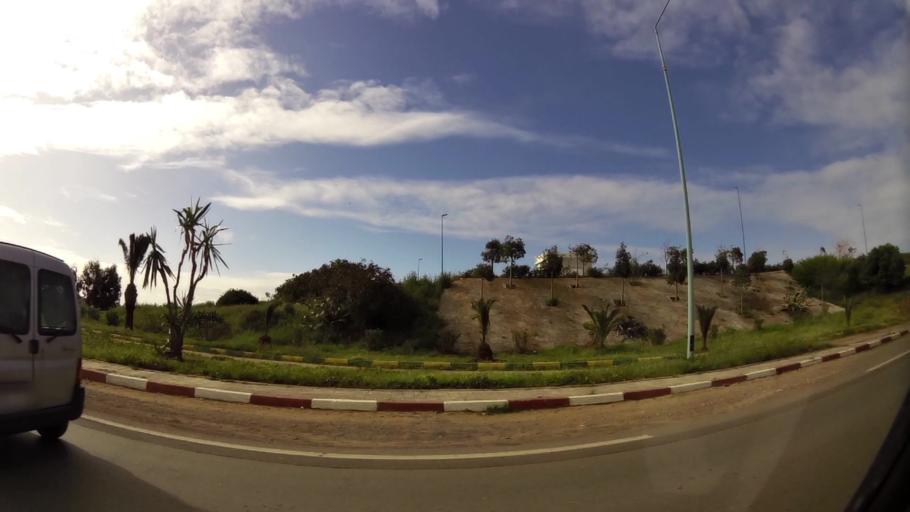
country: MA
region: Grand Casablanca
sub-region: Mohammedia
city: Mohammedia
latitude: 33.7151
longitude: -7.3377
